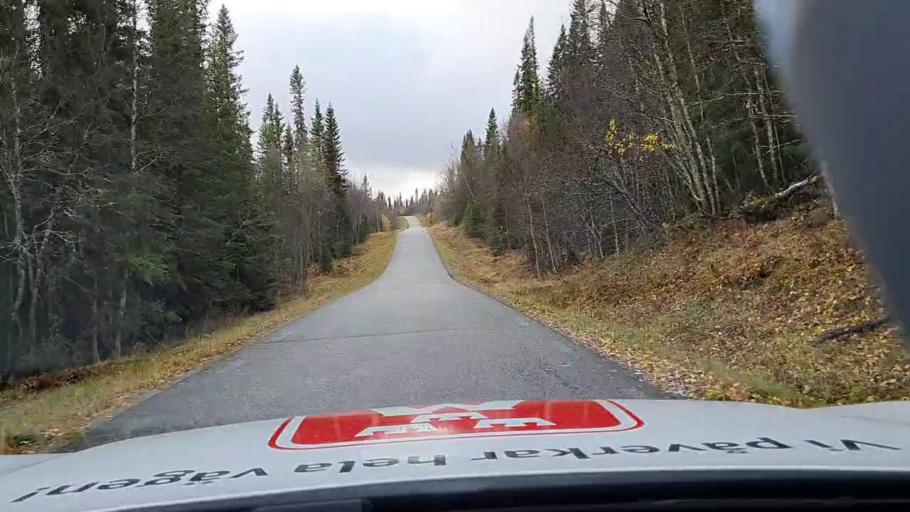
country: SE
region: Jaemtland
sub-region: Bergs Kommun
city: Hoverberg
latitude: 63.0144
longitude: 13.9424
